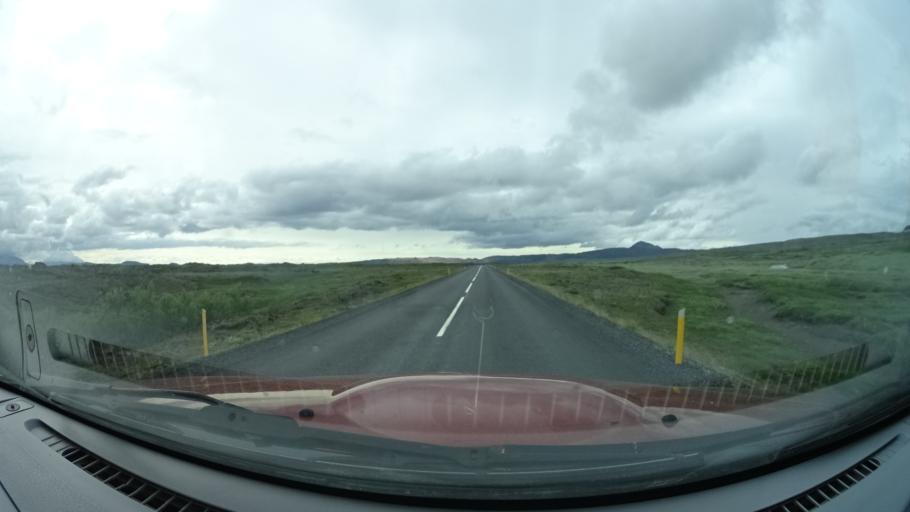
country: IS
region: Northeast
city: Laugar
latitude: 65.6444
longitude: -16.6840
